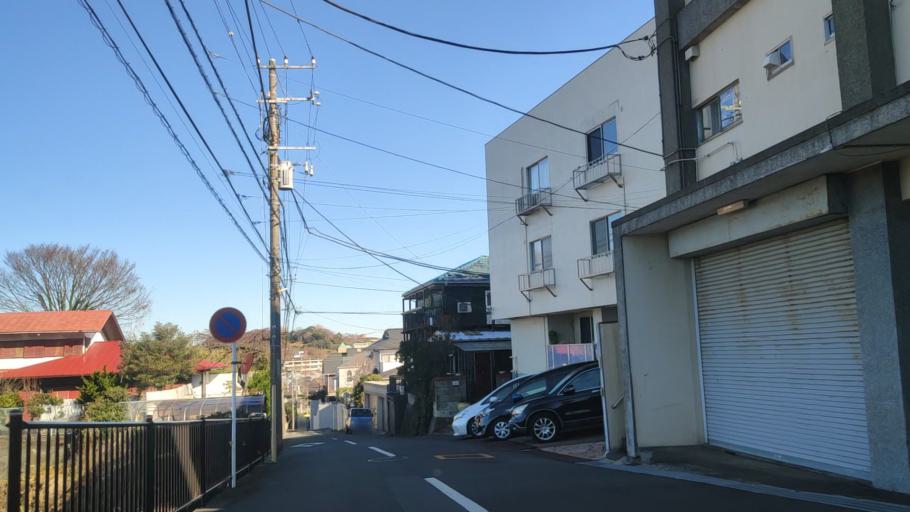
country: JP
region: Kanagawa
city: Yokohama
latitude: 35.4196
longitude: 139.6591
